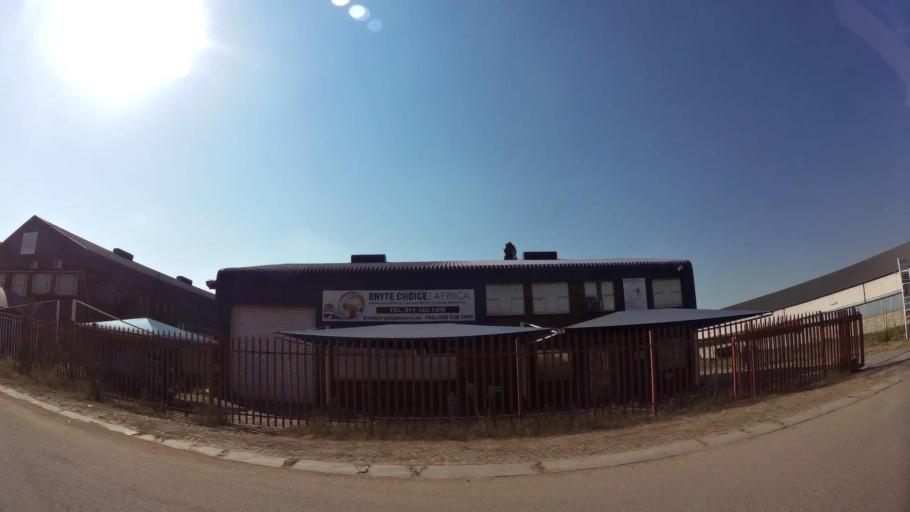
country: ZA
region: Gauteng
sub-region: Ekurhuleni Metropolitan Municipality
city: Benoni
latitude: -26.2012
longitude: 28.3149
